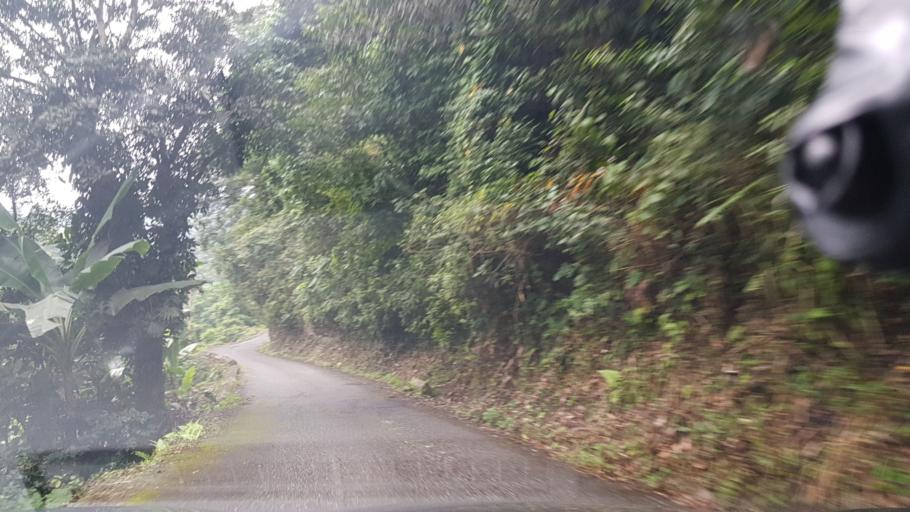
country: JM
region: Saint Andrew
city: Stony Hill
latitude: 18.1201
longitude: -76.7160
